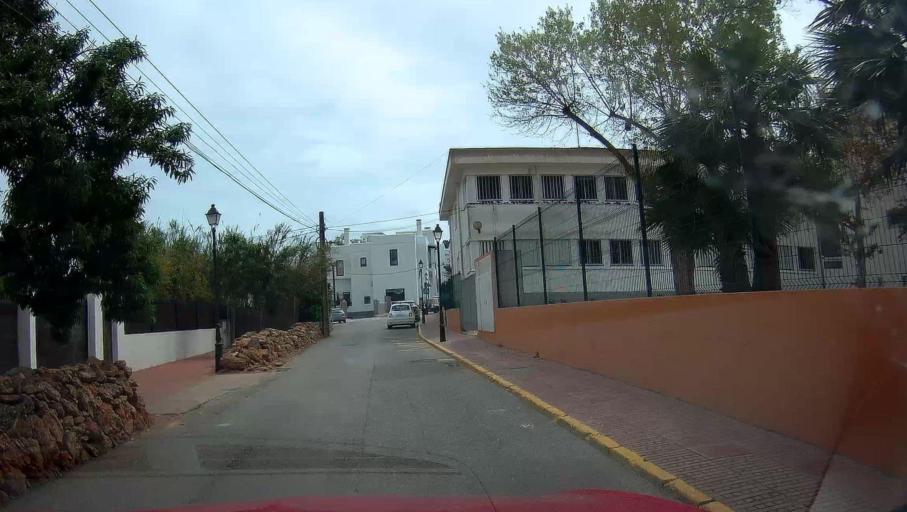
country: ES
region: Balearic Islands
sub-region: Illes Balears
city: Ibiza
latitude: 38.9998
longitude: 1.4293
